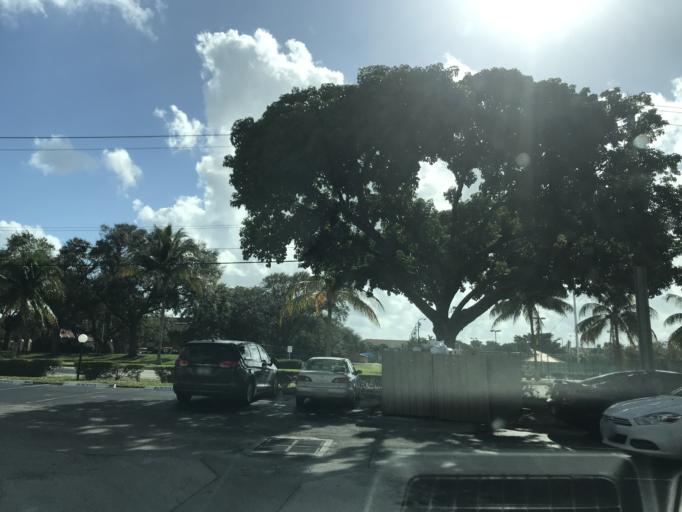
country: US
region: Florida
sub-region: Broward County
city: Margate
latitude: 26.2659
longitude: -80.1990
